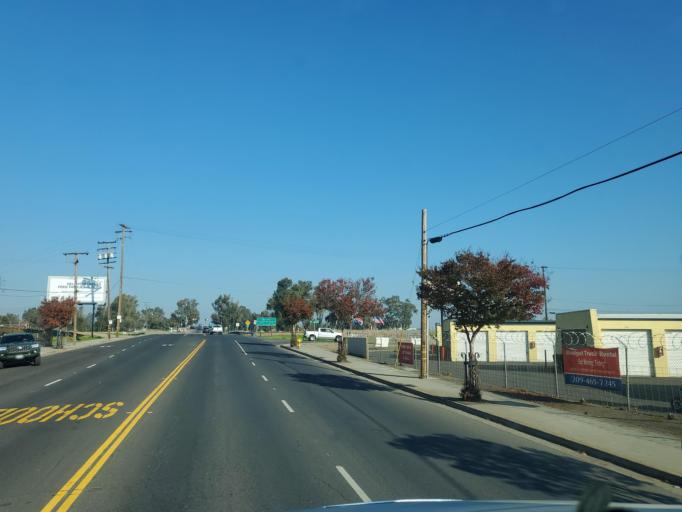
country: US
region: California
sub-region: San Joaquin County
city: August
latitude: 37.9821
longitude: -121.2540
